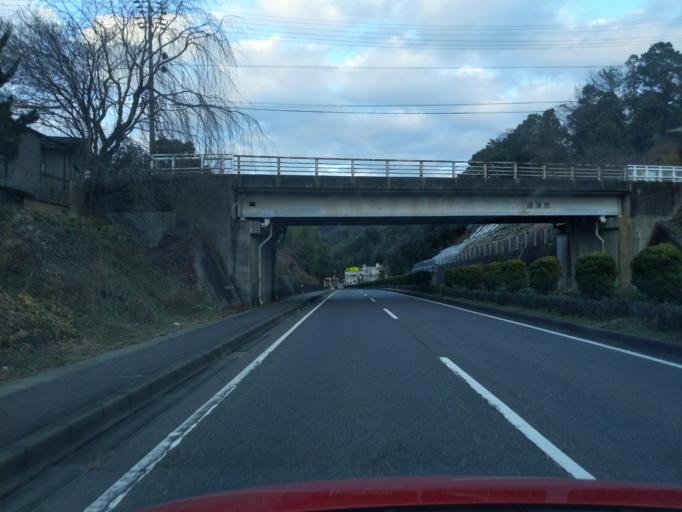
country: JP
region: Gifu
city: Mizunami
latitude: 35.3587
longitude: 137.2583
